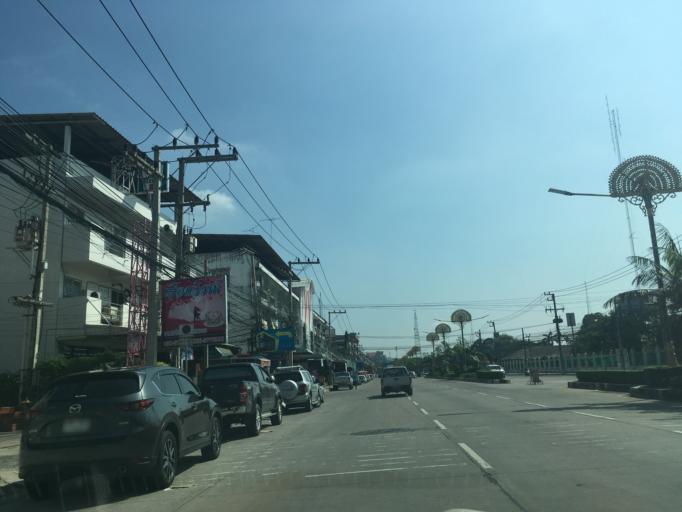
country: TH
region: Chon Buri
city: Chon Buri
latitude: 13.3529
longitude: 100.9762
